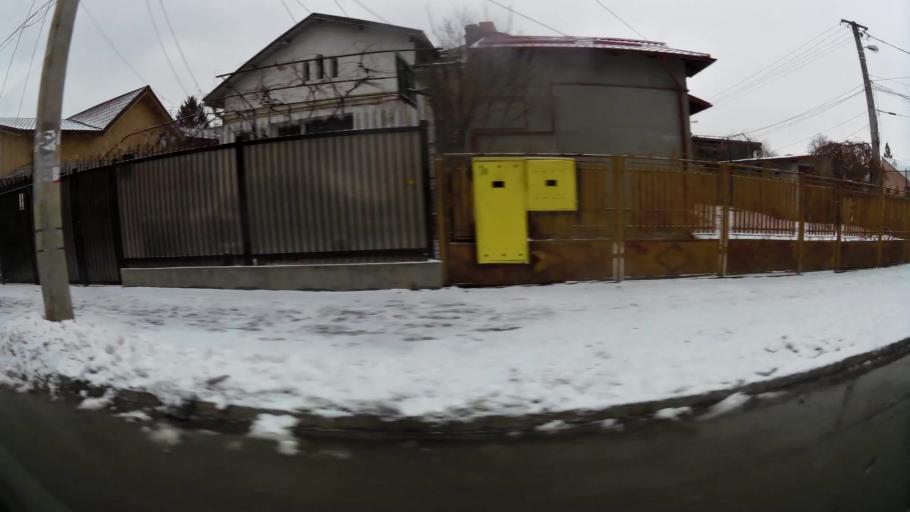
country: RO
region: Prahova
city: Ploiesti
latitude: 44.9295
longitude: 26.0408
